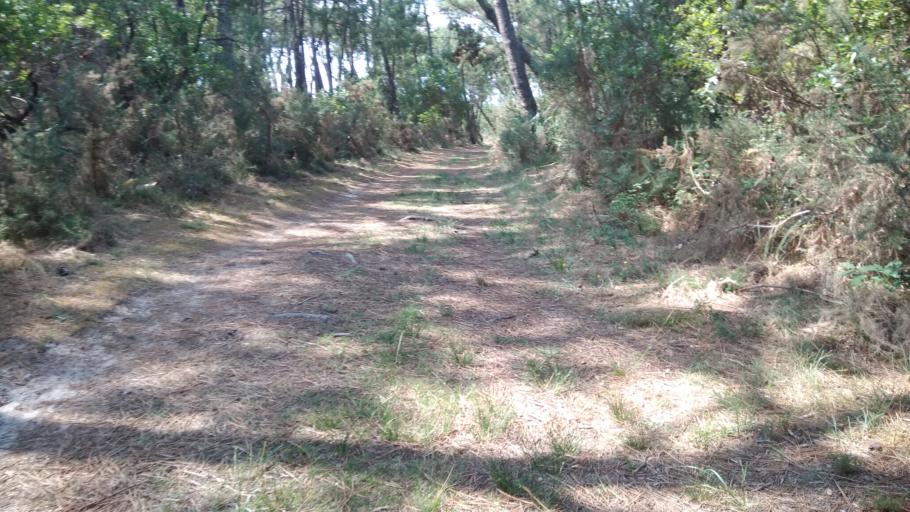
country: FR
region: Aquitaine
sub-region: Departement des Landes
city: Mimizan
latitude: 44.1976
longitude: -1.2962
